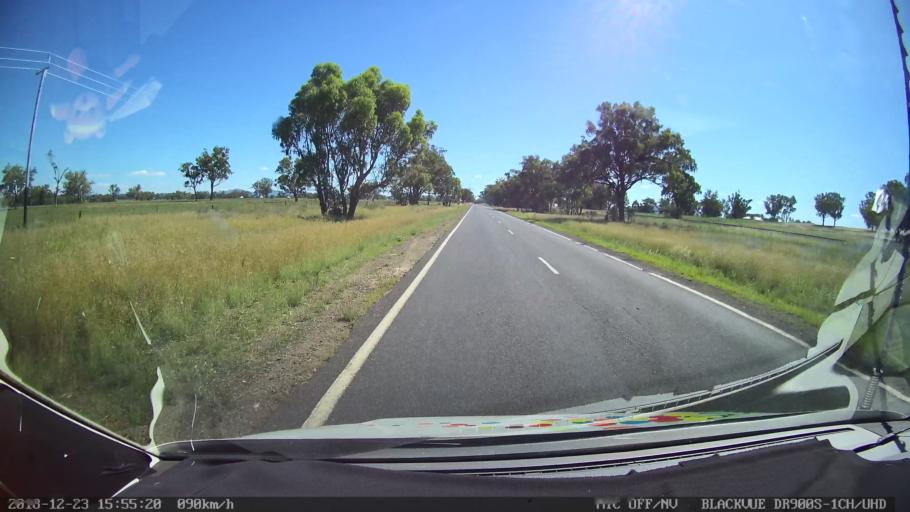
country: AU
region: New South Wales
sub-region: Tamworth Municipality
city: Phillip
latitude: -31.1545
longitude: 150.8694
